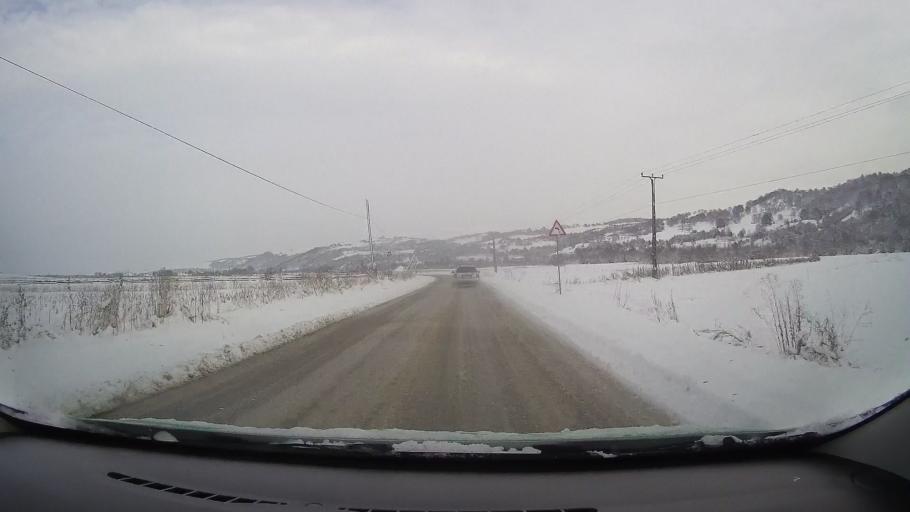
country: RO
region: Alba
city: Pianu de Sus
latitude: 45.9162
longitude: 23.4842
